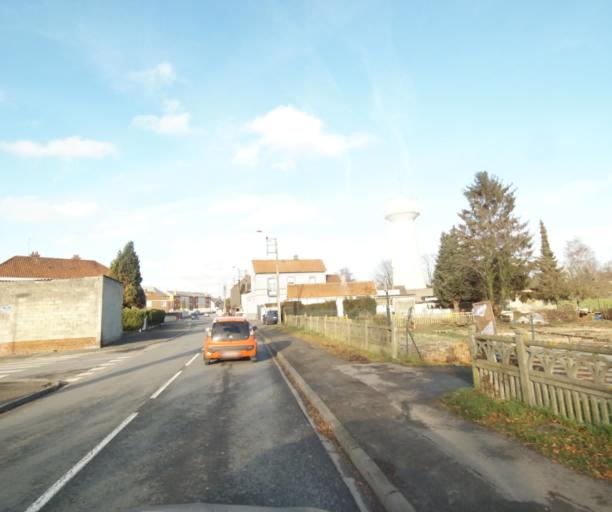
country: FR
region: Nord-Pas-de-Calais
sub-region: Departement du Nord
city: Valenciennes
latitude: 50.3592
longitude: 3.5411
